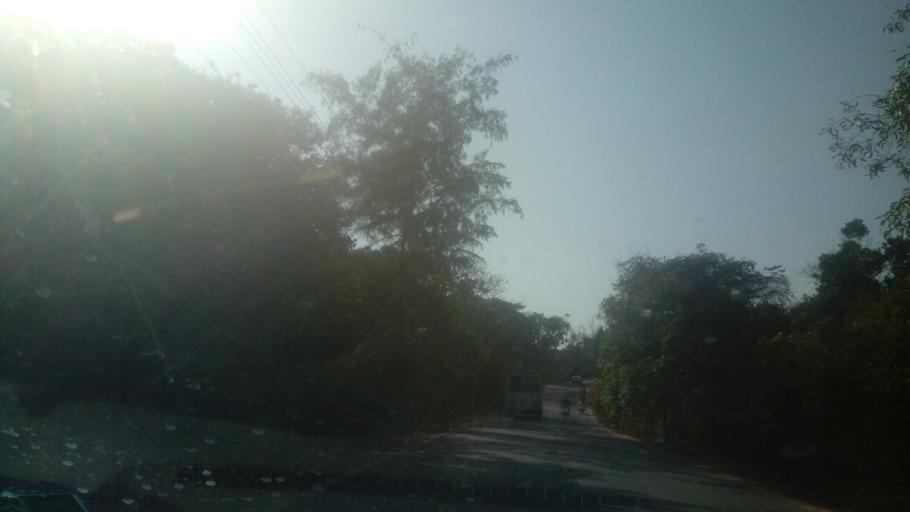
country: IN
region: Goa
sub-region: North Goa
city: Navelim
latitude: 15.5274
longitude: 73.9970
